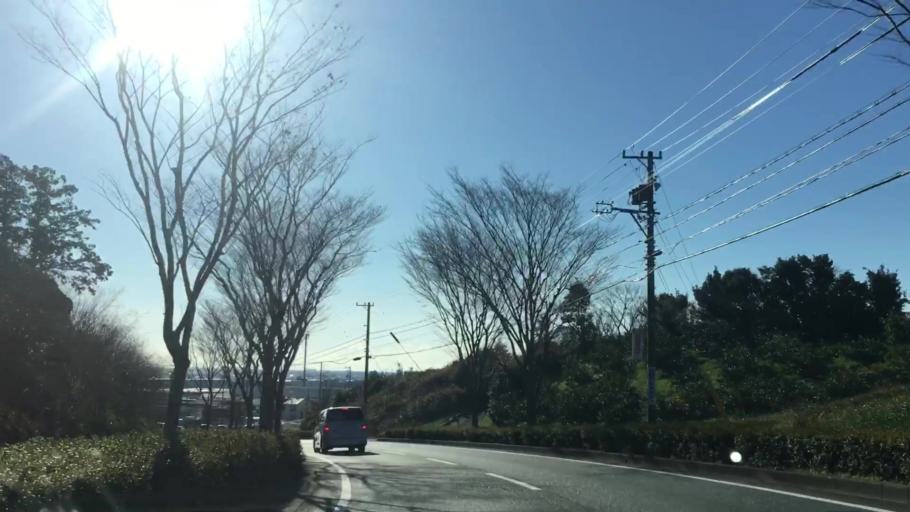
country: JP
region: Shizuoka
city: Hamakita
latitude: 34.8018
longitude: 137.7451
